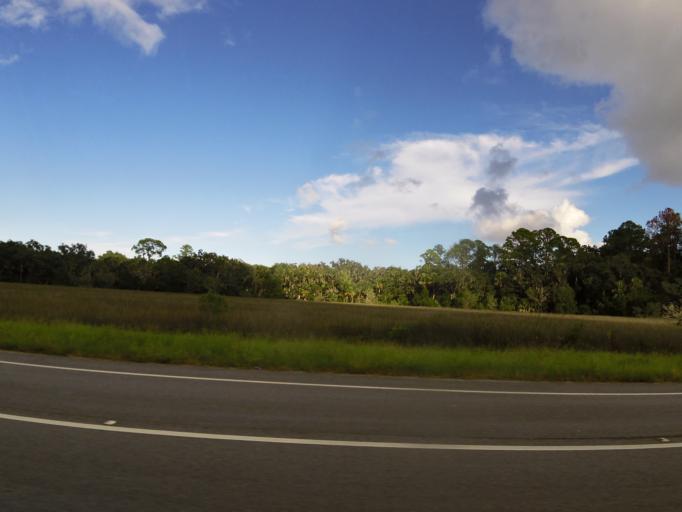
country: US
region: Georgia
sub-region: Glynn County
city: Country Club Estates
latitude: 31.1979
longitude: -81.4682
